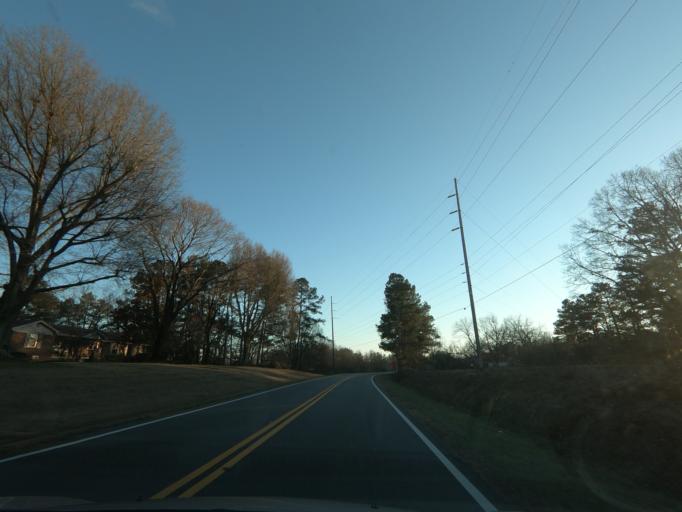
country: US
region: Georgia
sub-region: Forsyth County
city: Cumming
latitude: 34.3048
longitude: -84.1506
